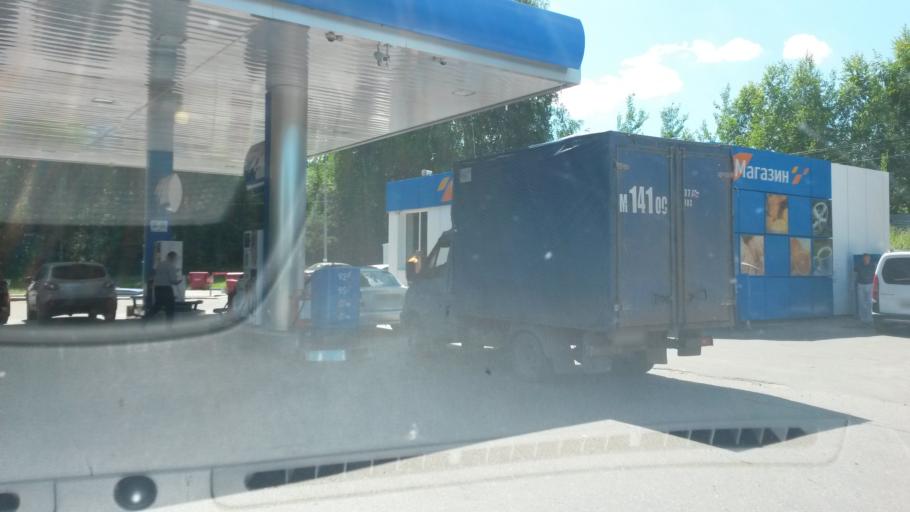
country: RU
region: Ivanovo
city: Kokhma
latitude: 56.9651
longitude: 41.0598
